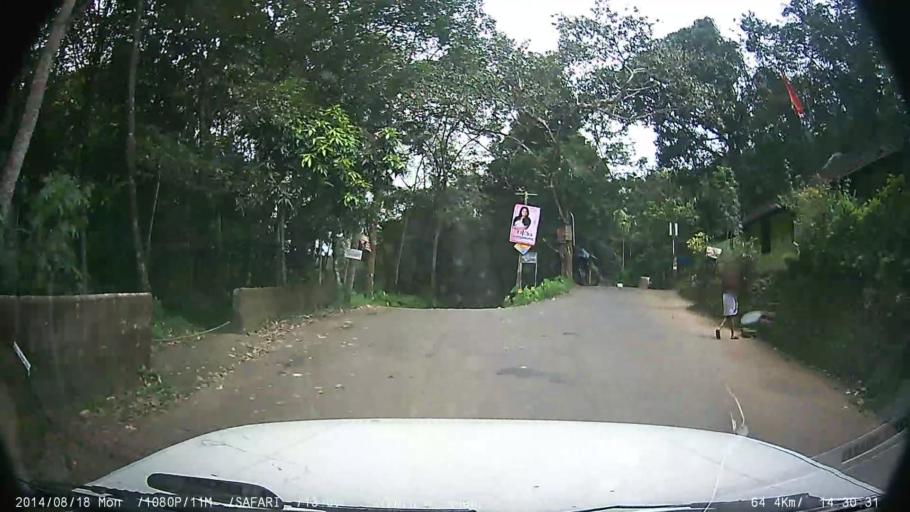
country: IN
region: Kerala
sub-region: Kottayam
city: Palackattumala
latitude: 9.7872
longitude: 76.5513
